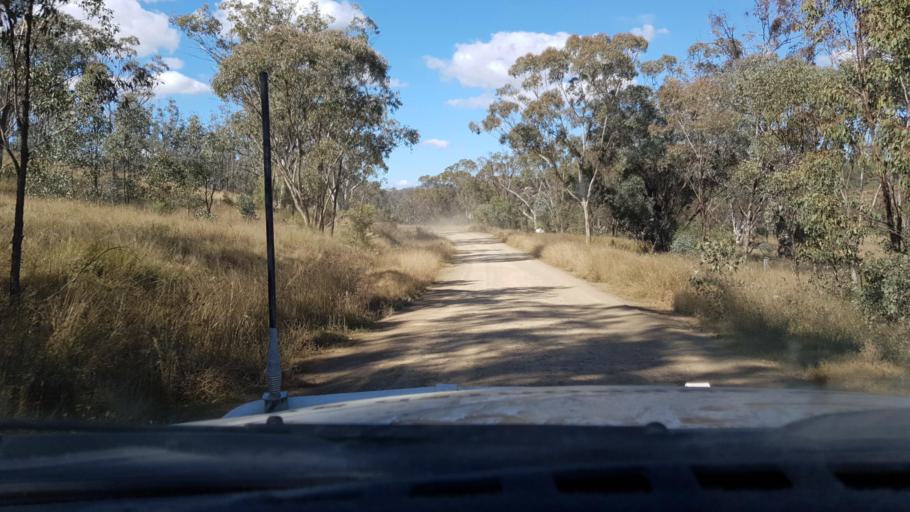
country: AU
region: New South Wales
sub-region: Tamworth Municipality
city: Manilla
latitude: -30.4773
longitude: 150.7605
